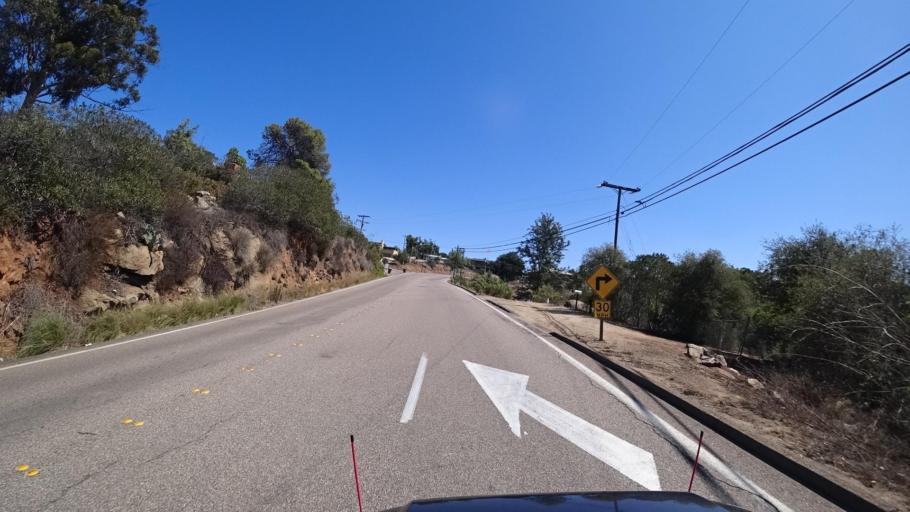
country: US
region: California
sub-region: San Diego County
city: Crest
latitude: 32.8148
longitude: -116.8653
